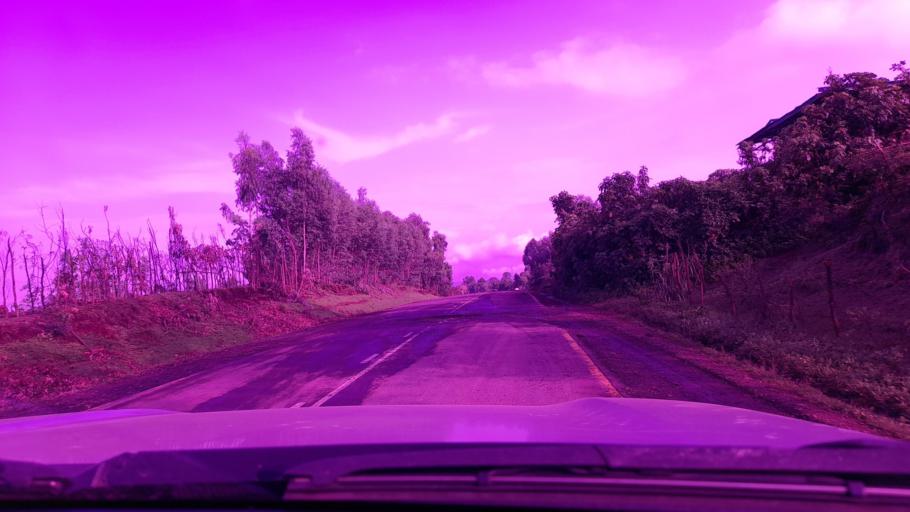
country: ET
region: Oromiya
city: Bedele
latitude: 8.1881
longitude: 36.4474
